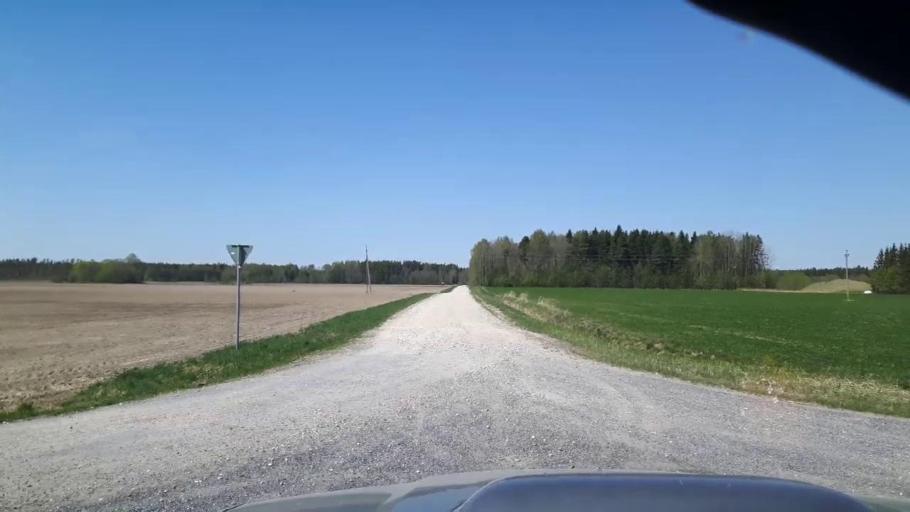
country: EE
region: Paernumaa
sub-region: Tootsi vald
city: Tootsi
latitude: 58.4693
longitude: 24.7735
